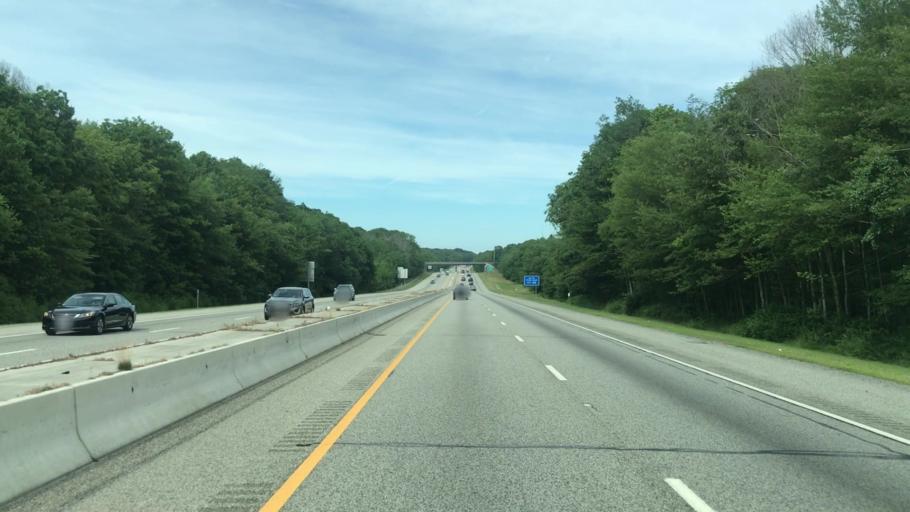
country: US
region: Rhode Island
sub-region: Washington County
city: Hopkinton
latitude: 41.4559
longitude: -71.7764
